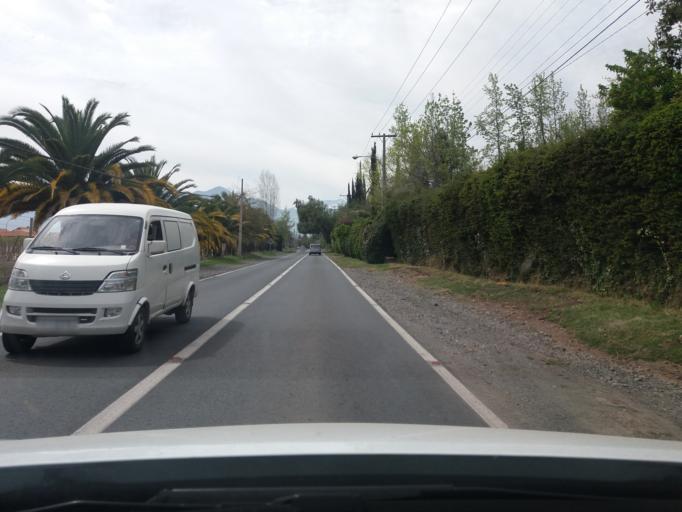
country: CL
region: Valparaiso
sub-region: Provincia de Los Andes
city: Los Andes
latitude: -32.8323
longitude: -70.6250
